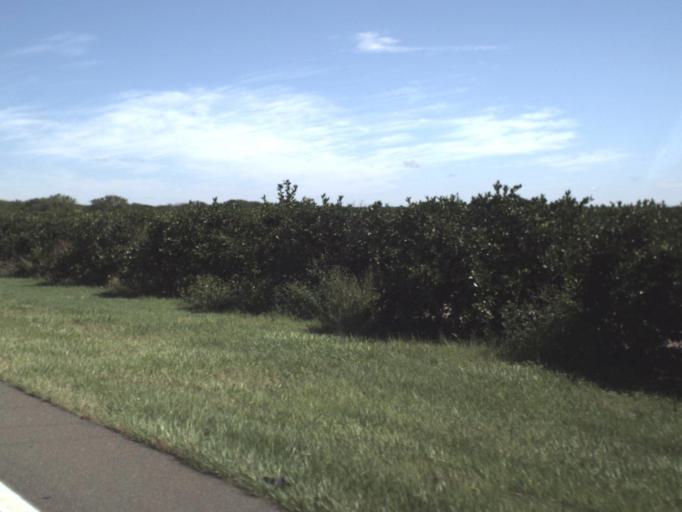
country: US
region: Florida
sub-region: Polk County
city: Auburndale
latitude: 28.1239
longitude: -81.7893
